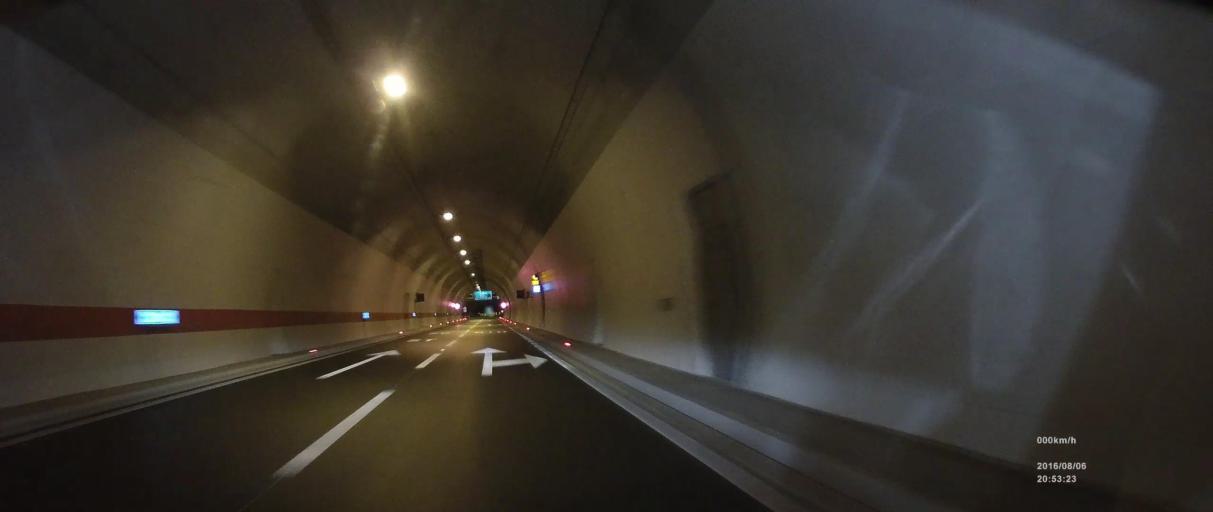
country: BA
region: Federation of Bosnia and Herzegovina
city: Ljubuski
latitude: 43.1423
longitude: 17.4870
